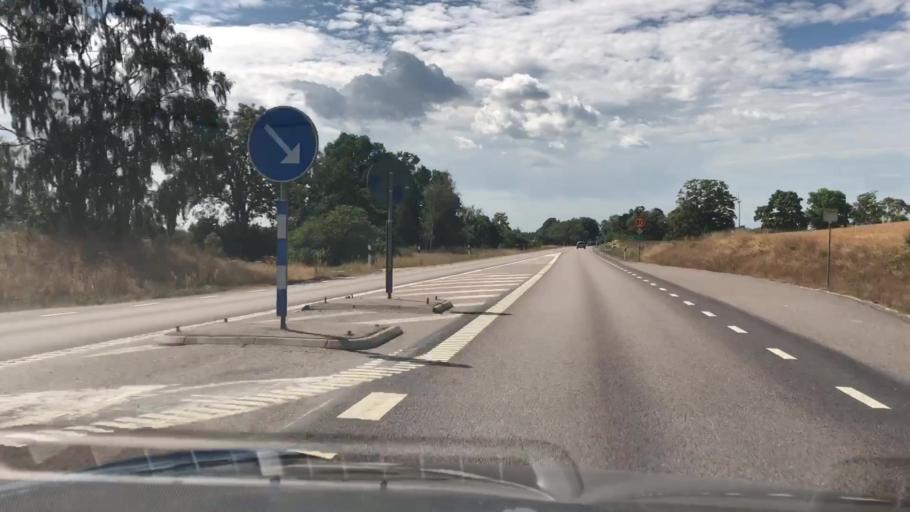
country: SE
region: Kalmar
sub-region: Torsas Kommun
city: Torsas
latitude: 56.4274
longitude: 16.0757
